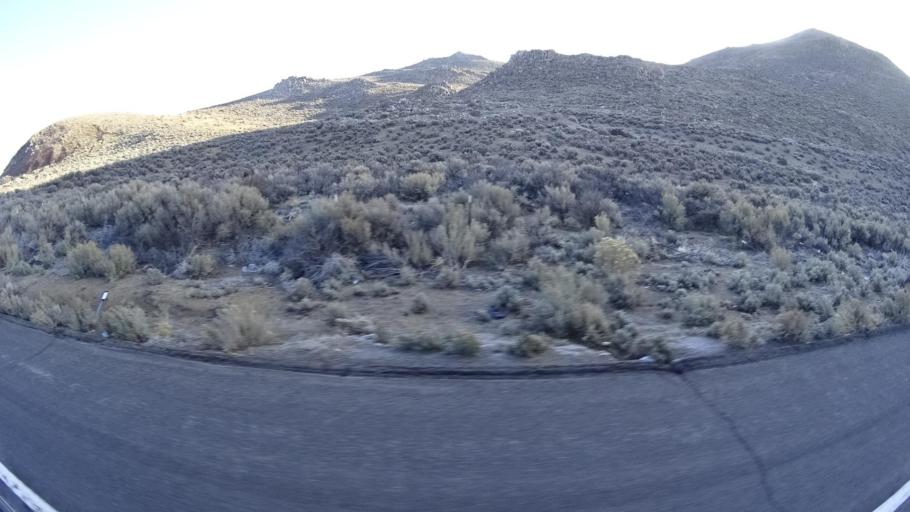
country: US
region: Nevada
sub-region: Washoe County
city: Cold Springs
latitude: 39.6601
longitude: -119.9594
